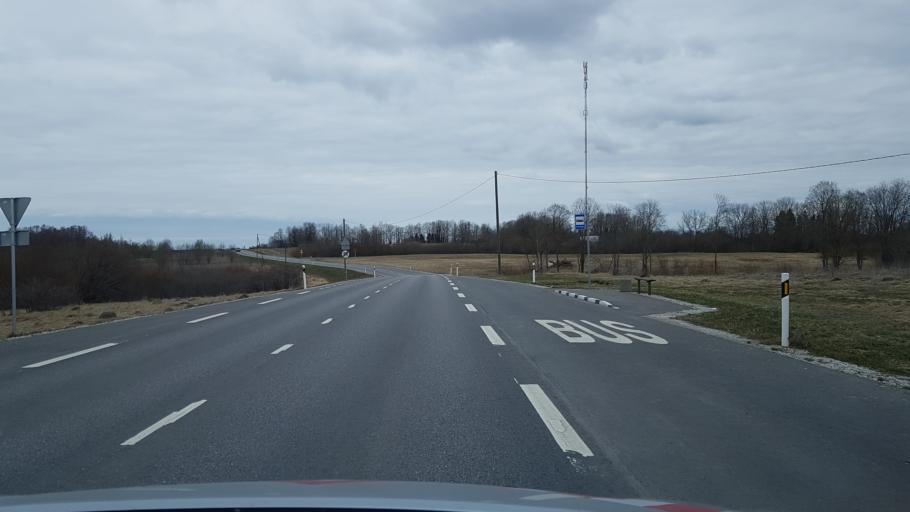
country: EE
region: Ida-Virumaa
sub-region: Narva-Joesuu linn
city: Narva-Joesuu
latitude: 59.4028
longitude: 28.0657
